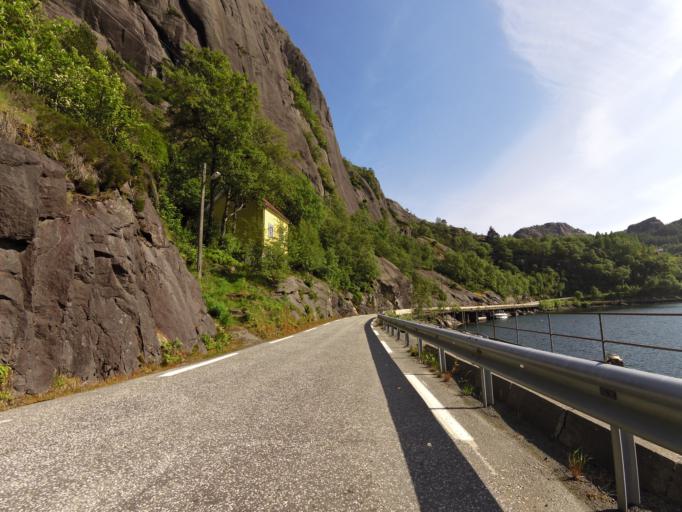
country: NO
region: Rogaland
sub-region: Sokndal
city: Hauge i Dalane
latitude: 58.3197
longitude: 6.3485
